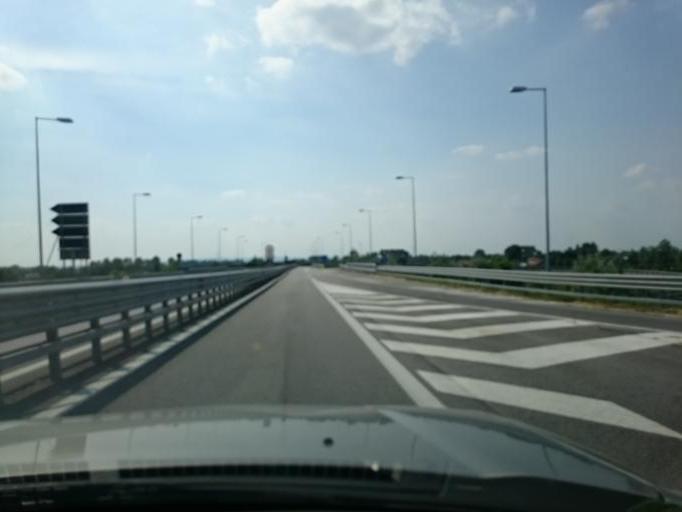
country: IT
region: Veneto
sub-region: Provincia di Padova
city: Tencarola
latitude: 45.3814
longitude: 11.8285
